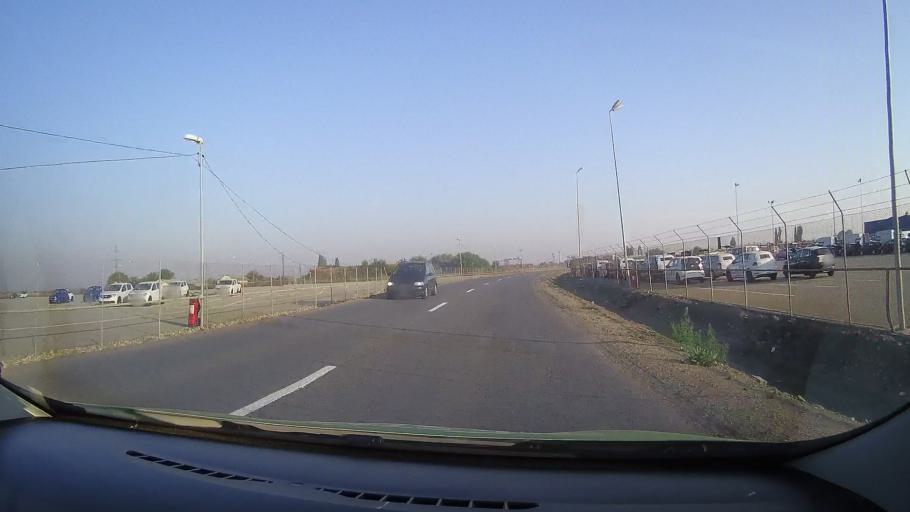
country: RO
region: Arad
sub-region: Comuna Curtici
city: Curtici
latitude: 46.3324
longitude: 21.2973
